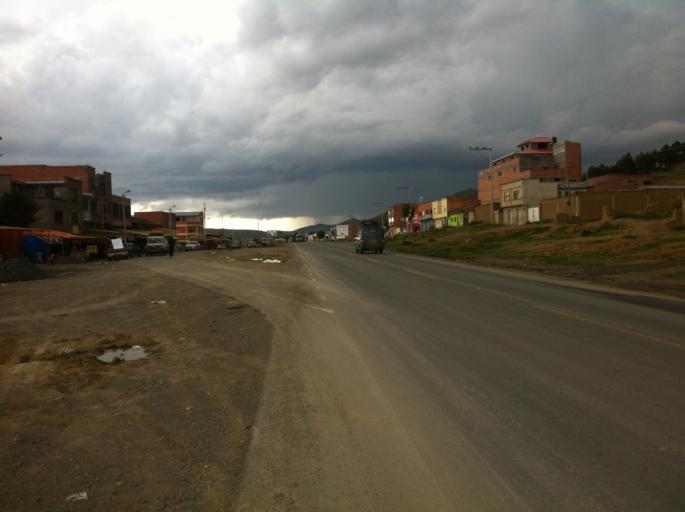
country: BO
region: La Paz
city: Huarina
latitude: -16.2010
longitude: -68.5978
